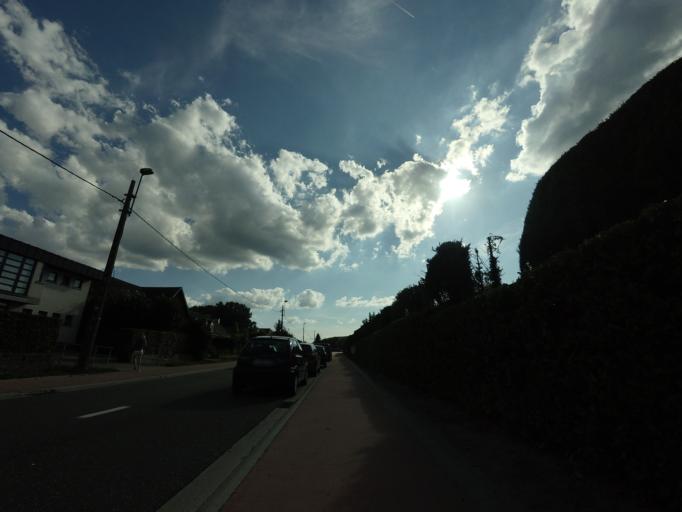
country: BE
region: Flanders
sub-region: Provincie Vlaams-Brabant
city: Kapelle-op-den-Bos
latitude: 50.9776
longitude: 4.3504
